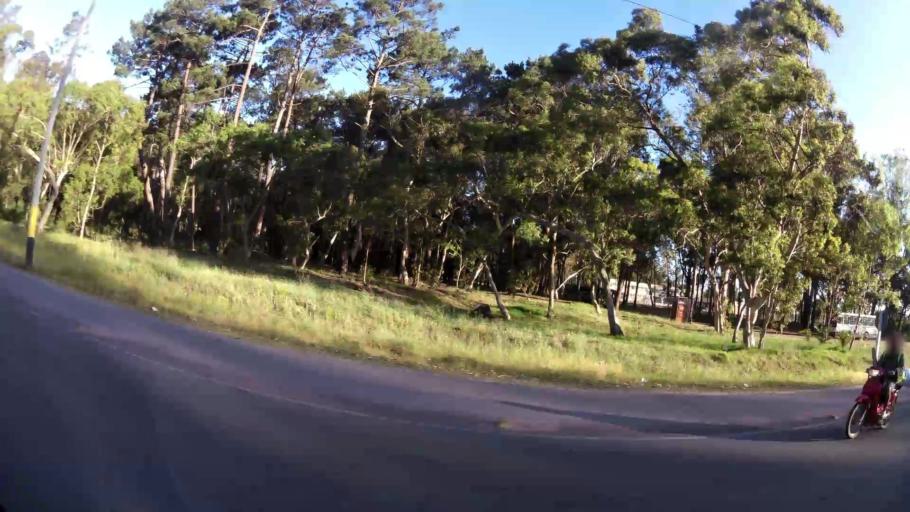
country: UY
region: Canelones
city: Paso de Carrasco
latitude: -34.8517
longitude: -56.0374
